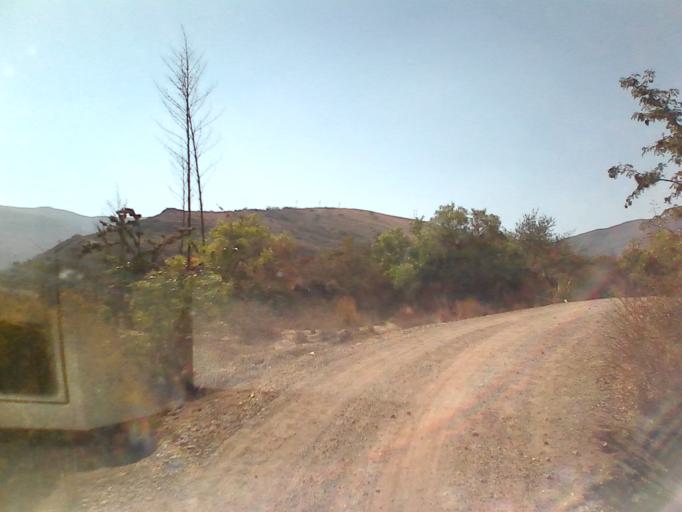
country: CO
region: Boyaca
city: Sachica
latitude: 5.5765
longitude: -73.5421
